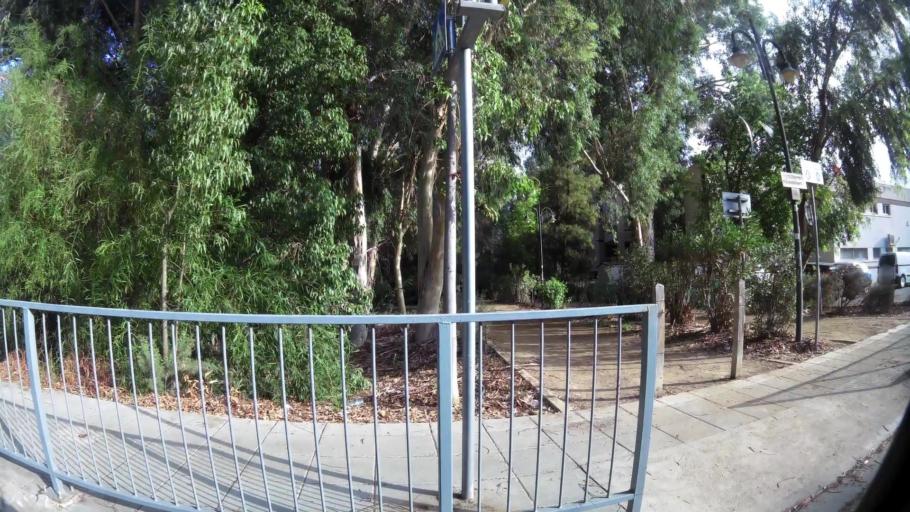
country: CY
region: Lefkosia
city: Nicosia
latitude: 35.1473
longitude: 33.3450
